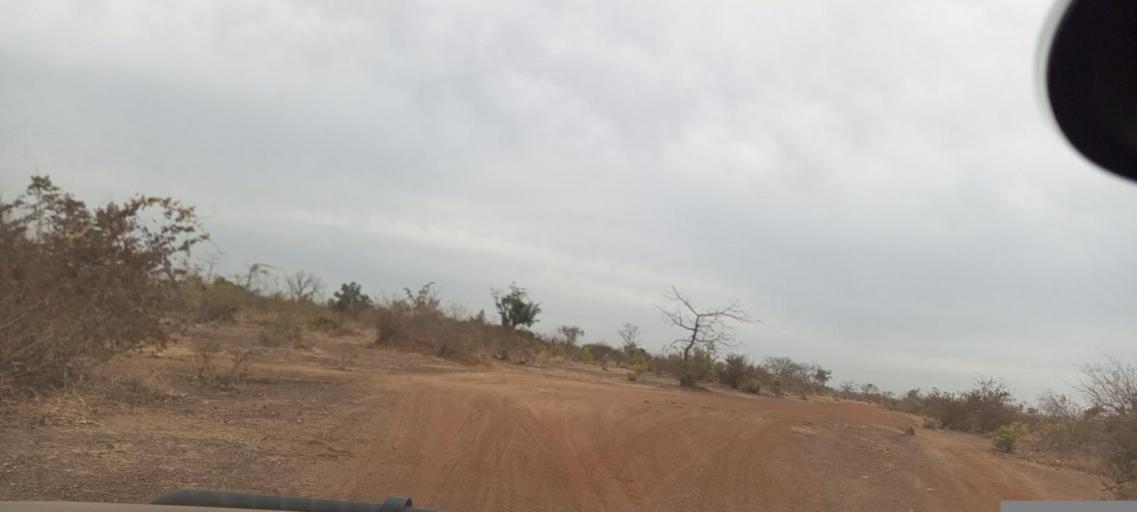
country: ML
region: Koulikoro
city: Kati
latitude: 12.7860
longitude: -8.2582
